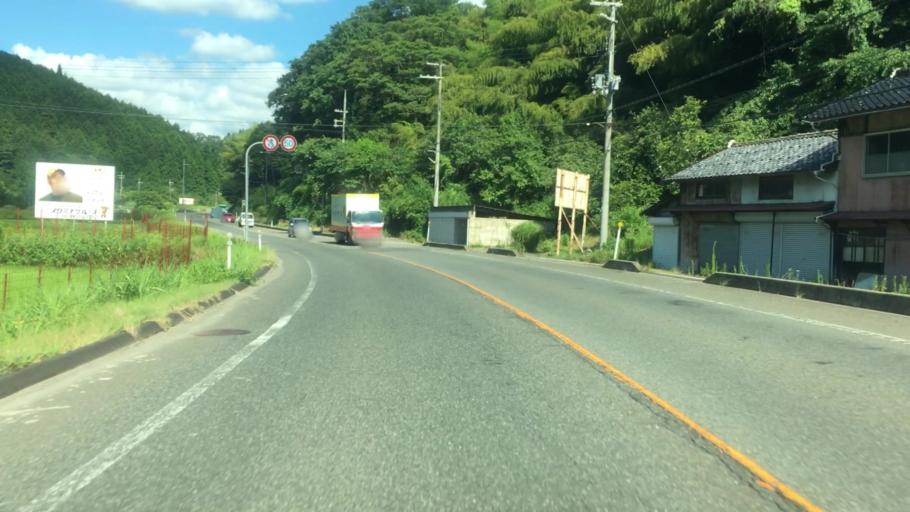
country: JP
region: Hyogo
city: Toyooka
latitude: 35.5716
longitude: 134.7789
